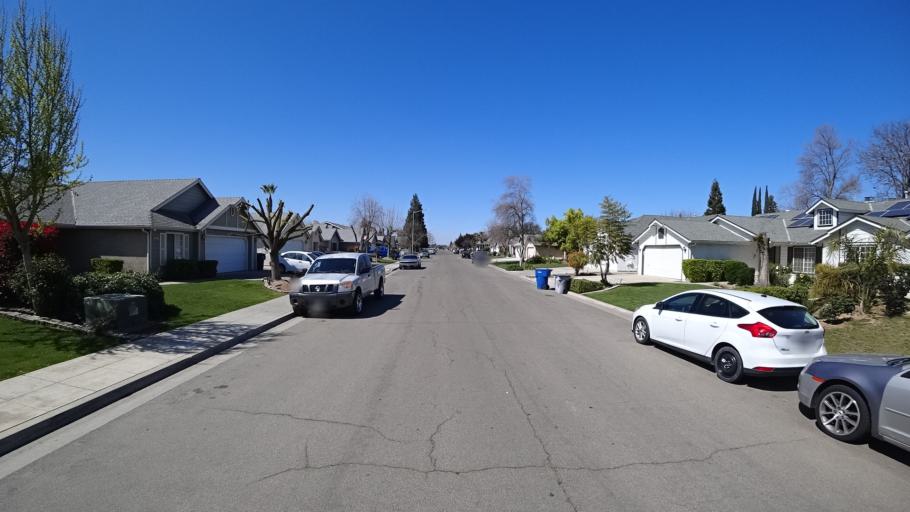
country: US
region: California
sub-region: Fresno County
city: West Park
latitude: 36.7830
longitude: -119.8866
